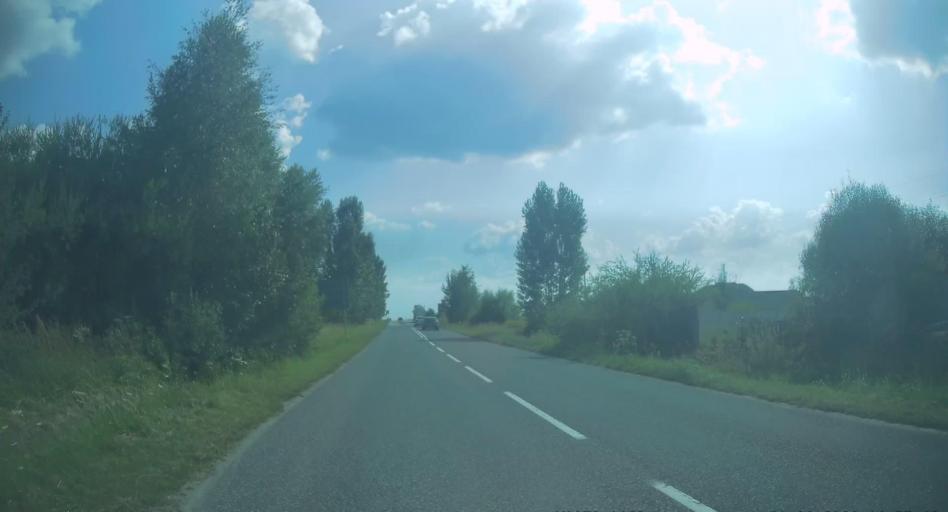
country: PL
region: Swietokrzyskie
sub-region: Powiat kielecki
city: Lopuszno
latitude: 50.9332
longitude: 20.2399
